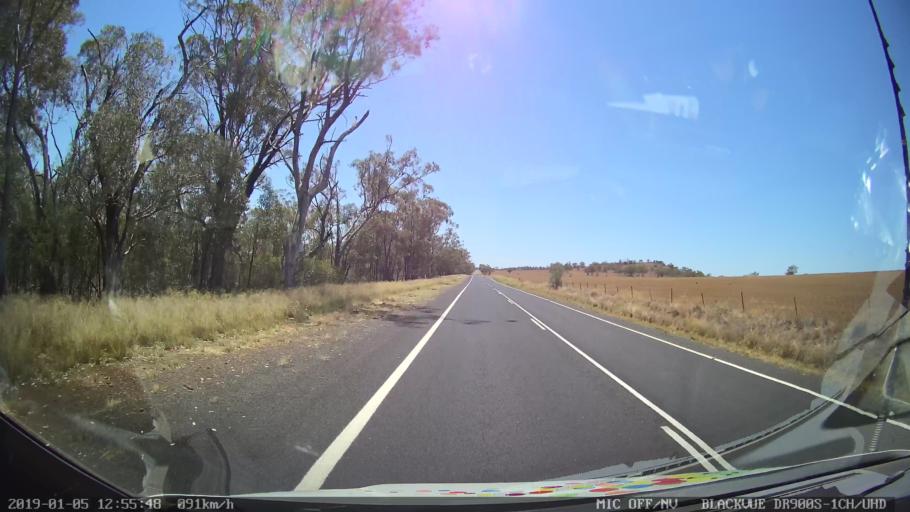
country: AU
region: New South Wales
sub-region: Warrumbungle Shire
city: Coonabarabran
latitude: -31.1191
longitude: 149.7114
